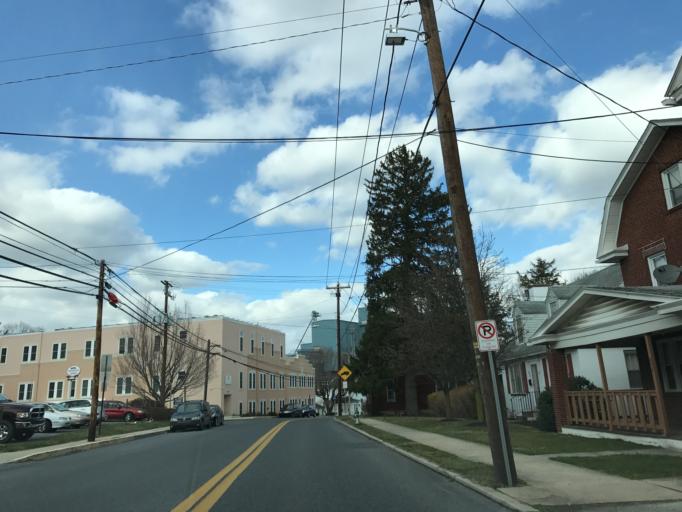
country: US
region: Pennsylvania
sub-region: Lancaster County
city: Elizabethtown
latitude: 40.1478
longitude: -76.6136
